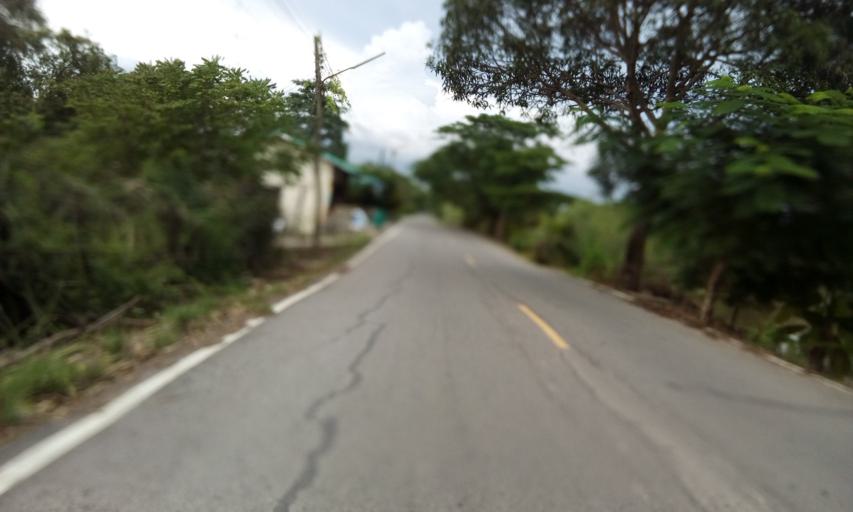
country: TH
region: Pathum Thani
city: Nong Suea
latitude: 14.1939
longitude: 100.8230
